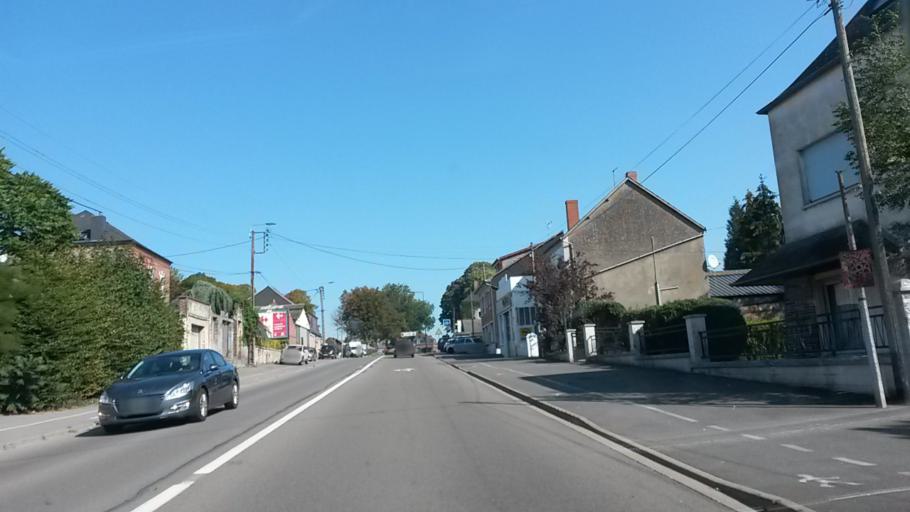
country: FR
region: Nord-Pas-de-Calais
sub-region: Departement du Nord
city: Avesnes-sur-Helpe
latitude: 50.1172
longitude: 3.9321
